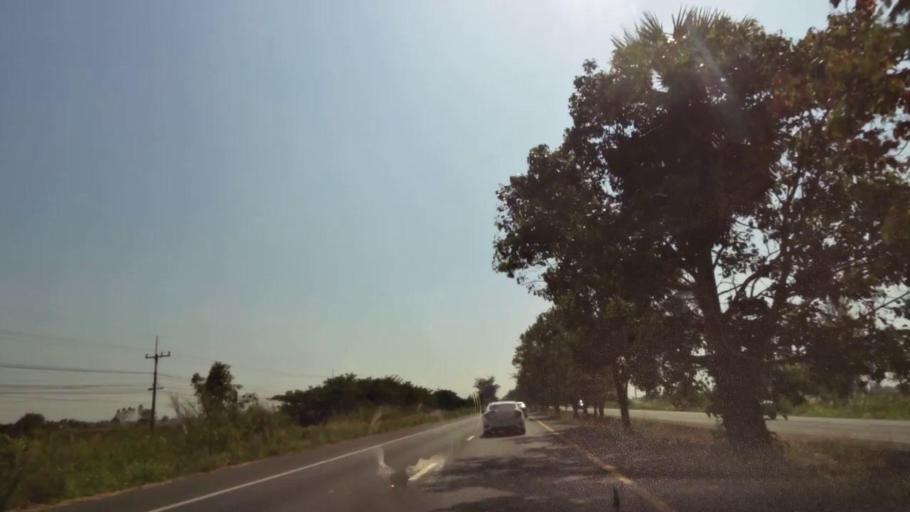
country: TH
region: Nakhon Sawan
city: Kao Liao
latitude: 15.9209
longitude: 100.1120
